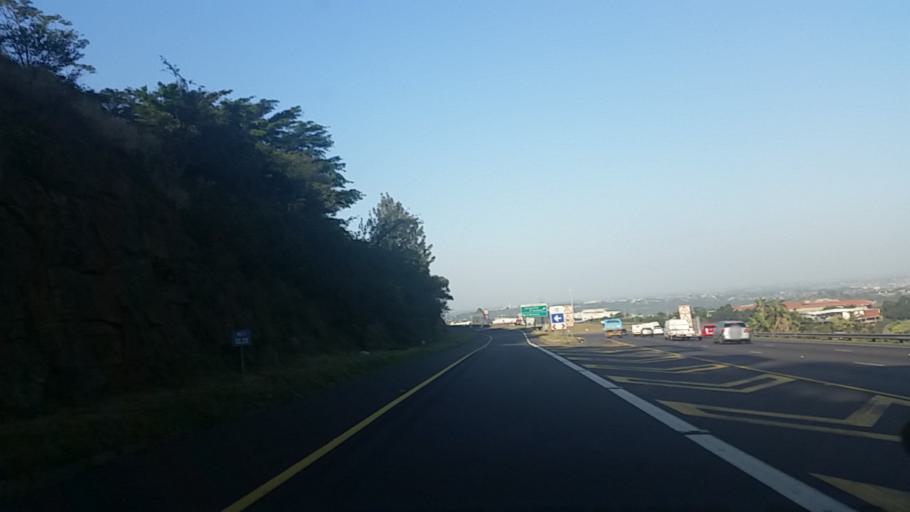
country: ZA
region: KwaZulu-Natal
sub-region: eThekwini Metropolitan Municipality
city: Berea
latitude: -29.8466
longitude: 30.9268
